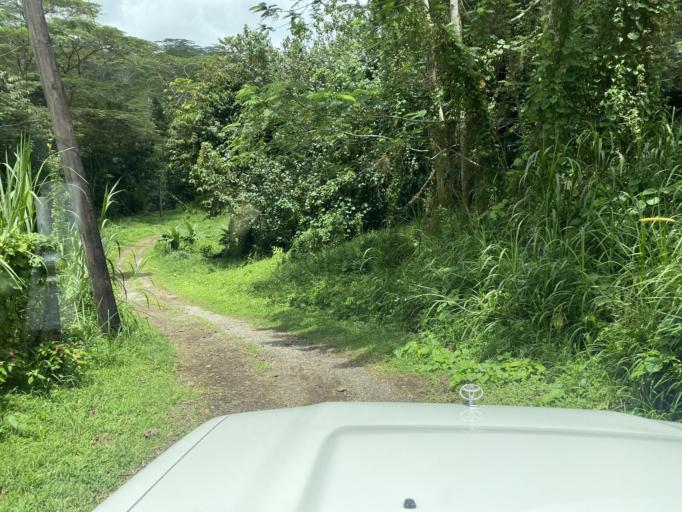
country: WS
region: Tuamasaga
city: Apia
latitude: -13.8977
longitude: -171.7744
